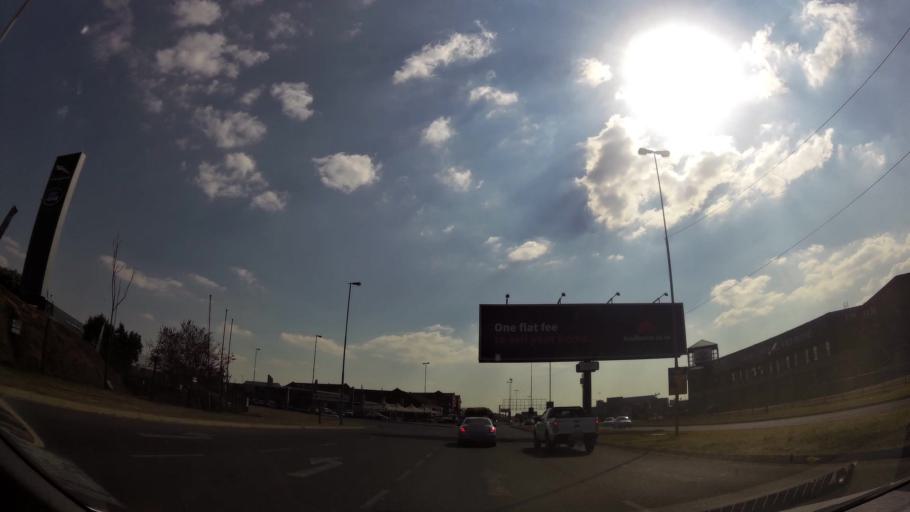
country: ZA
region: Gauteng
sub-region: Ekurhuleni Metropolitan Municipality
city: Boksburg
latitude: -26.1818
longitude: 28.2448
